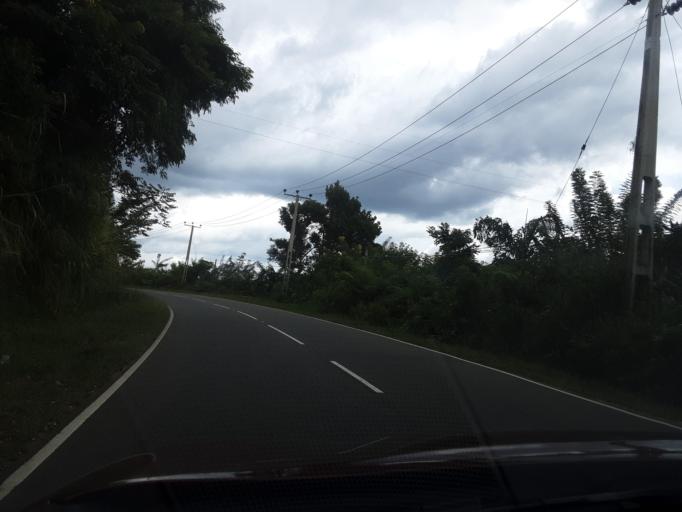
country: LK
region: Uva
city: Monaragala
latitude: 6.9087
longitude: 81.2135
